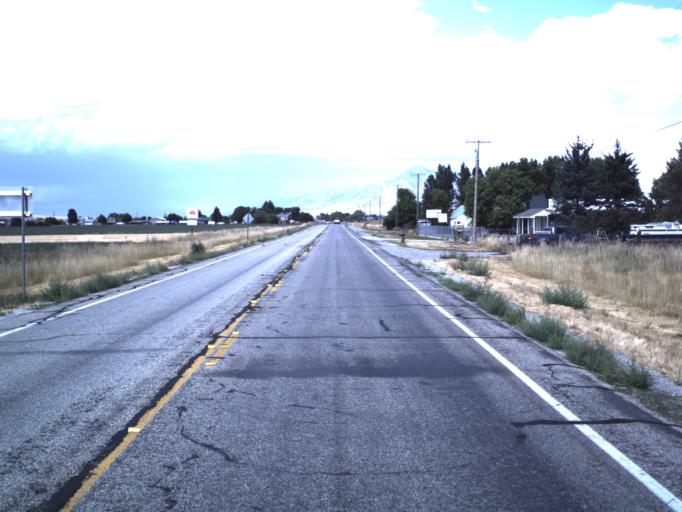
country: US
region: Utah
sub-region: Box Elder County
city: Garland
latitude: 41.7500
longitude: -112.1484
